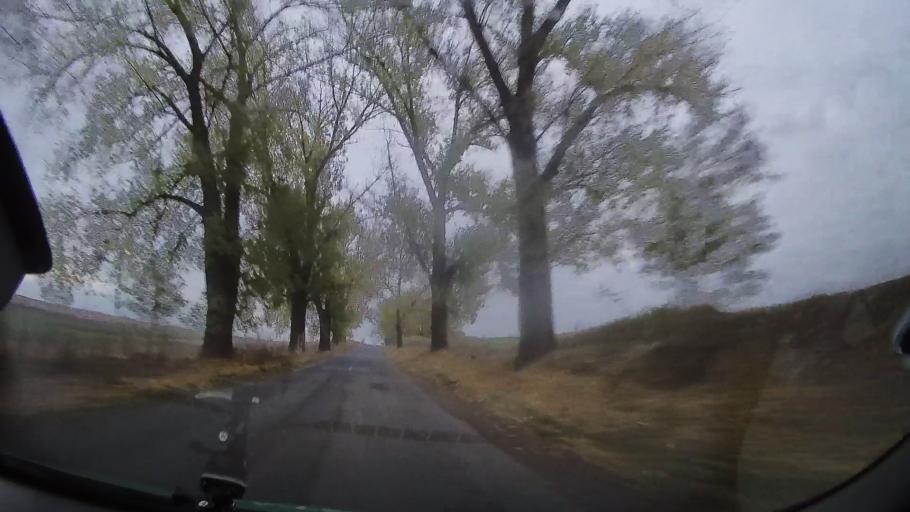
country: RO
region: Tulcea
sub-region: Comuna Mihai Bravu
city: Turda
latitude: 44.9665
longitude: 28.6325
